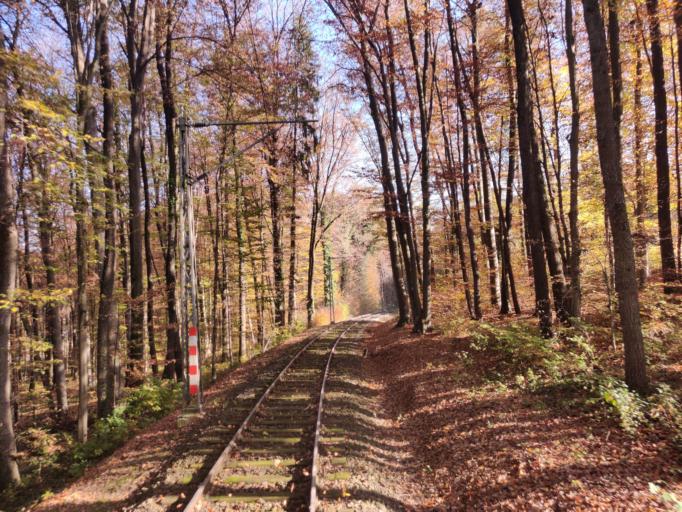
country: AT
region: Styria
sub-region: Politischer Bezirk Suedoststeiermark
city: Trautmannsdorf in Oststeiermark
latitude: 46.8778
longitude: 15.8907
